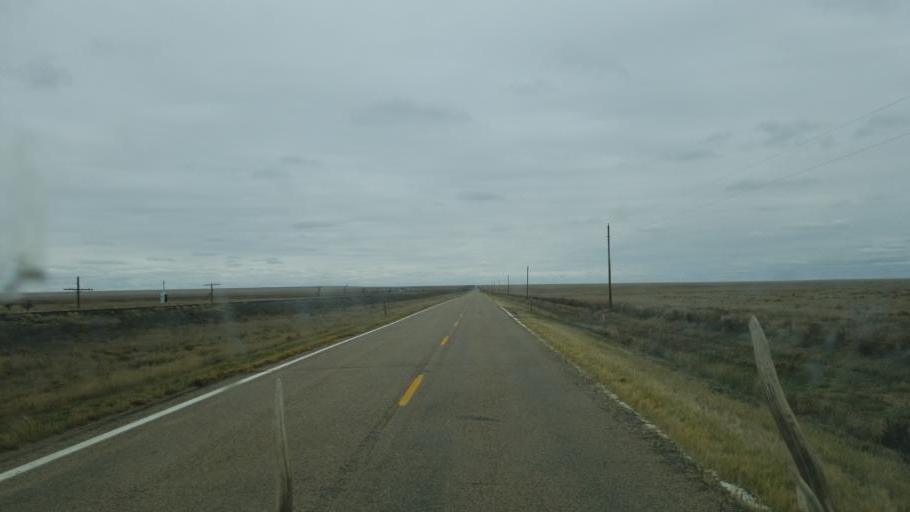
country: US
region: Colorado
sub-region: Crowley County
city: Ordway
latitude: 38.2438
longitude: -103.6129
